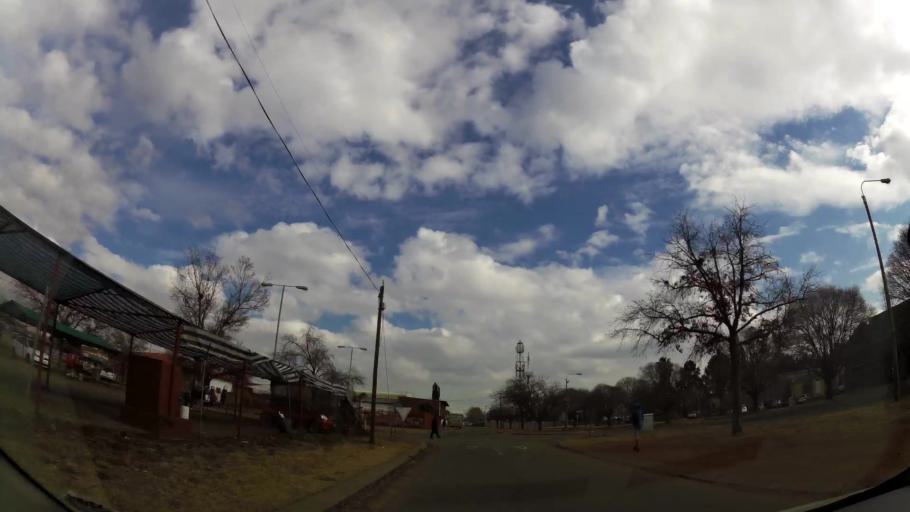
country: ZA
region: Gauteng
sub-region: Sedibeng District Municipality
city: Meyerton
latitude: -26.5582
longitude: 28.0160
